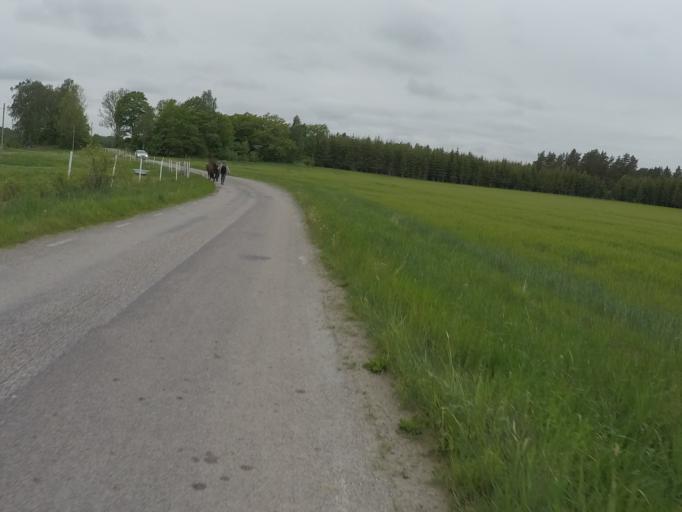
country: SE
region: Vaestmanland
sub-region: Hallstahammars Kommun
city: Kolback
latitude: 59.5478
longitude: 16.3025
